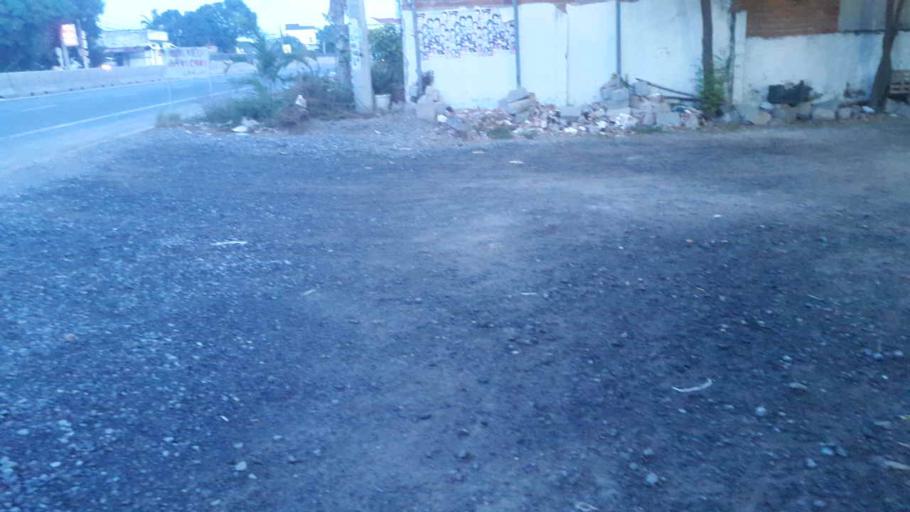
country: VN
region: Khanh Hoa
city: Cam Lam
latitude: 12.0791
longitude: 109.1563
